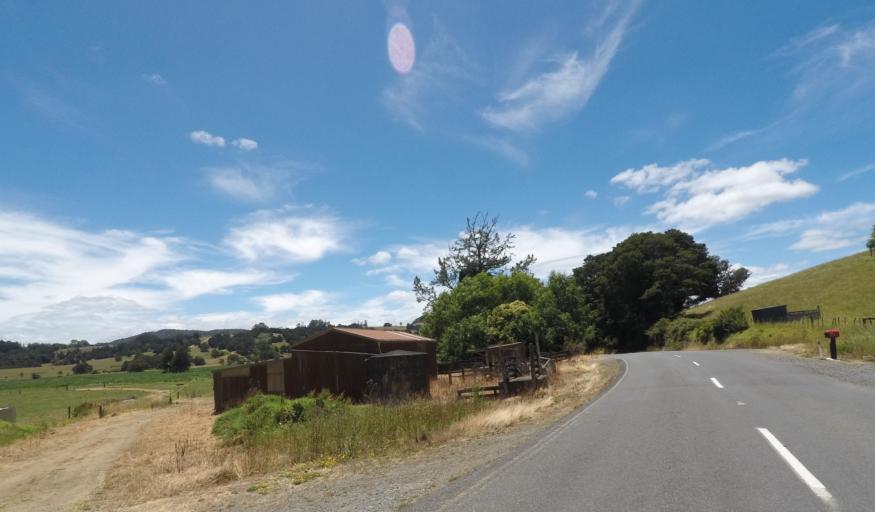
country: NZ
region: Northland
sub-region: Whangarei
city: Whangarei
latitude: -35.5359
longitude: 174.3135
